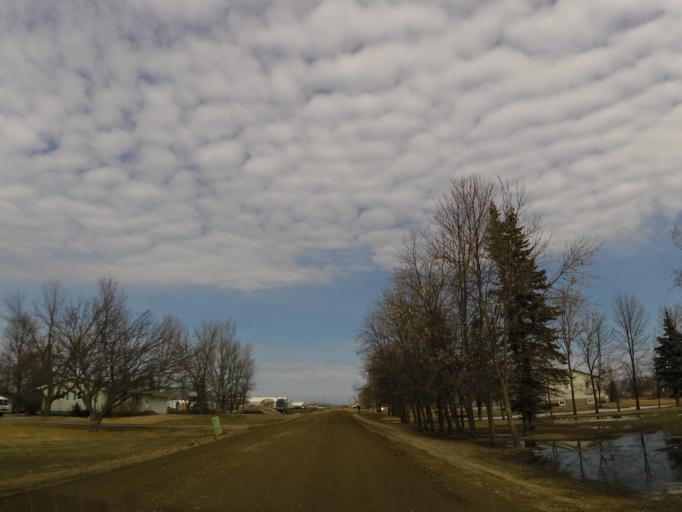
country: US
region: North Dakota
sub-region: Walsh County
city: Grafton
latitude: 48.2922
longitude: -97.3834
